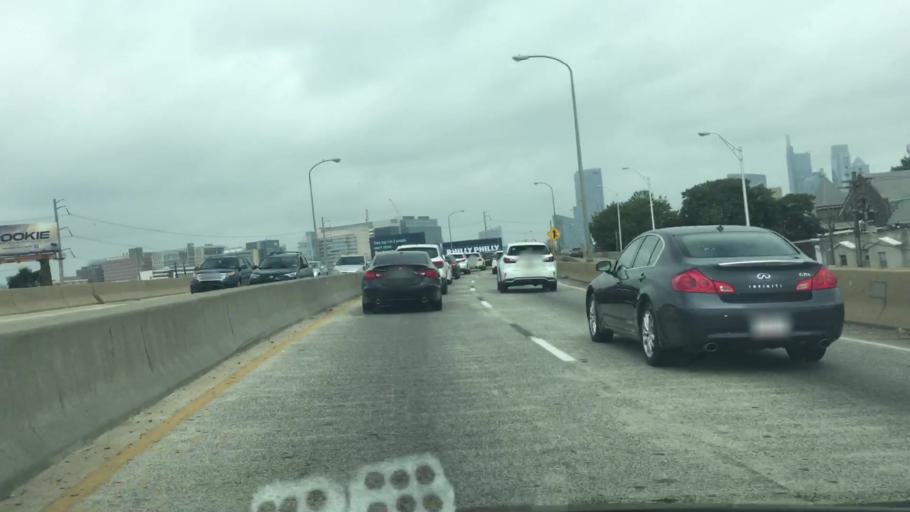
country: US
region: Pennsylvania
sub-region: Philadelphia County
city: Philadelphia
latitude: 39.9365
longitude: -75.1994
